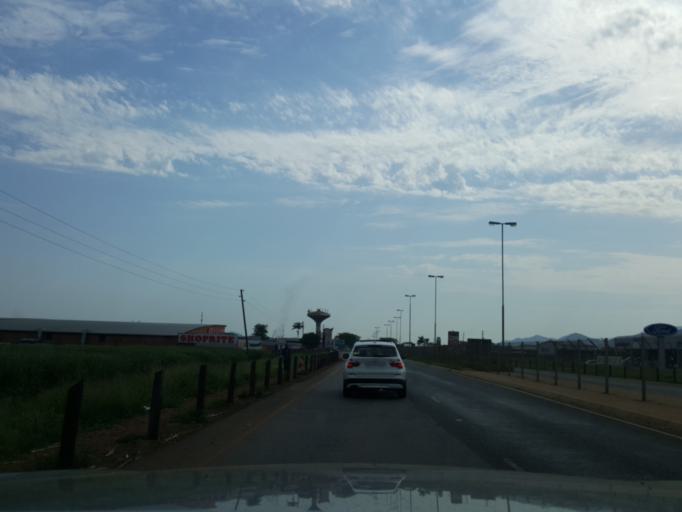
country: SZ
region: Hhohho
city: Ntfonjeni
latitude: -25.5016
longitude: 31.5044
